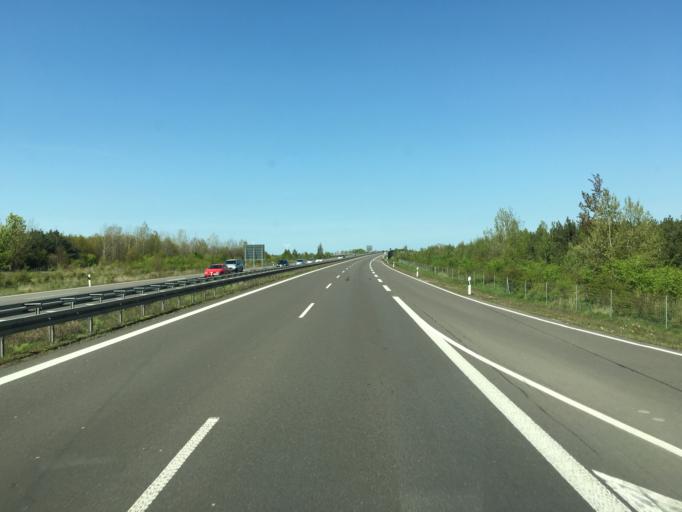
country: DE
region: Saxony
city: Zwenkau
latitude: 51.2523
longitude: 12.3056
